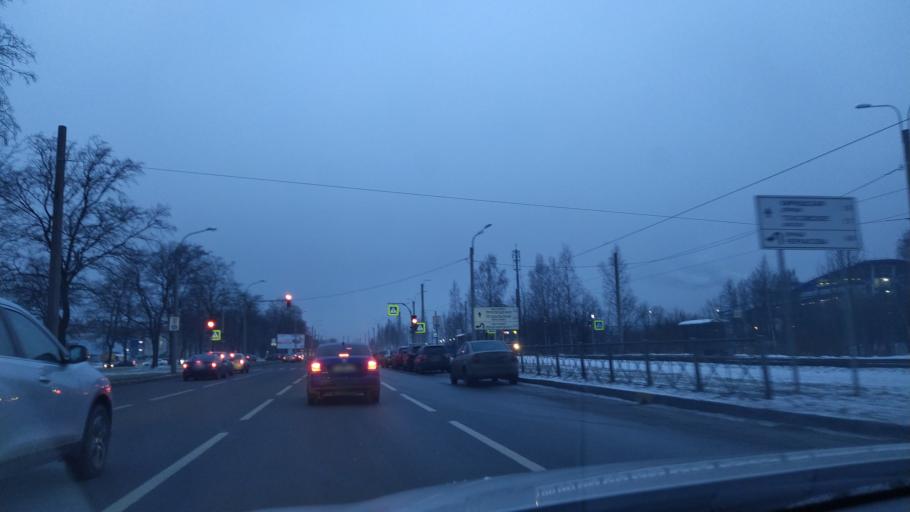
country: RU
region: St.-Petersburg
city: Grazhdanka
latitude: 60.0216
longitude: 30.4324
